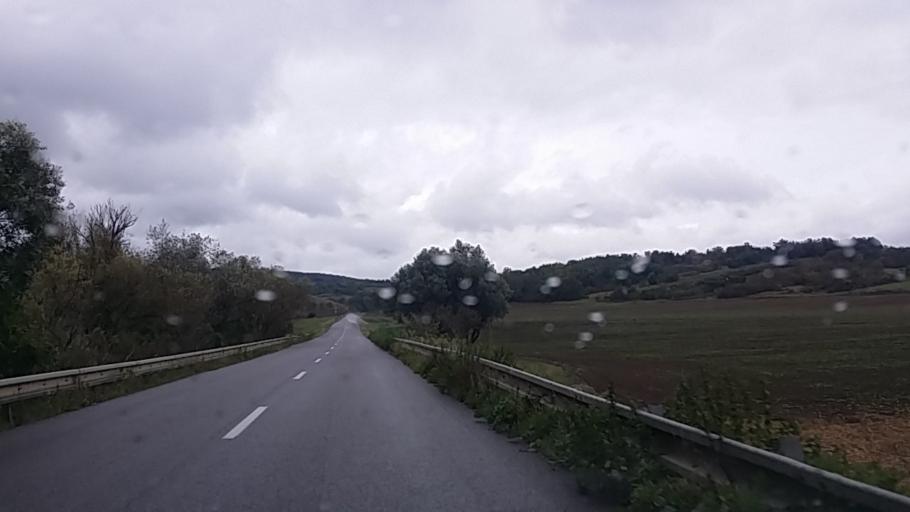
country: HU
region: Komarom-Esztergom
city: Esztergom
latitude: 47.8712
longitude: 18.7522
